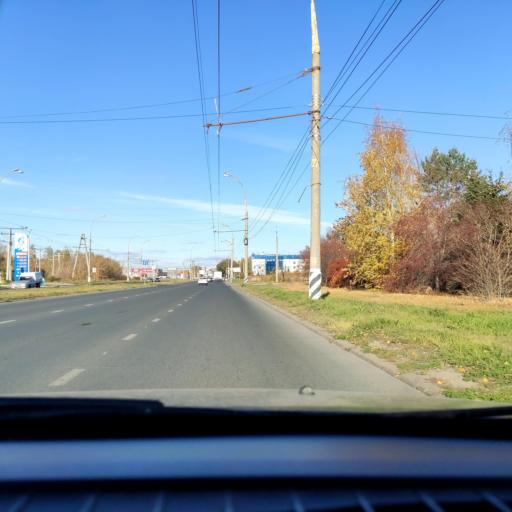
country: RU
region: Samara
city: Tol'yatti
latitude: 53.5496
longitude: 49.3024
